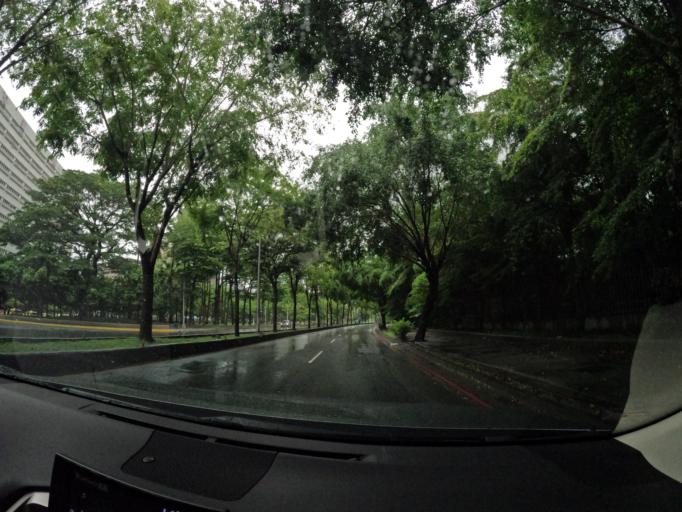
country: TW
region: Taiwan
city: Fengshan
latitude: 22.6507
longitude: 120.3544
